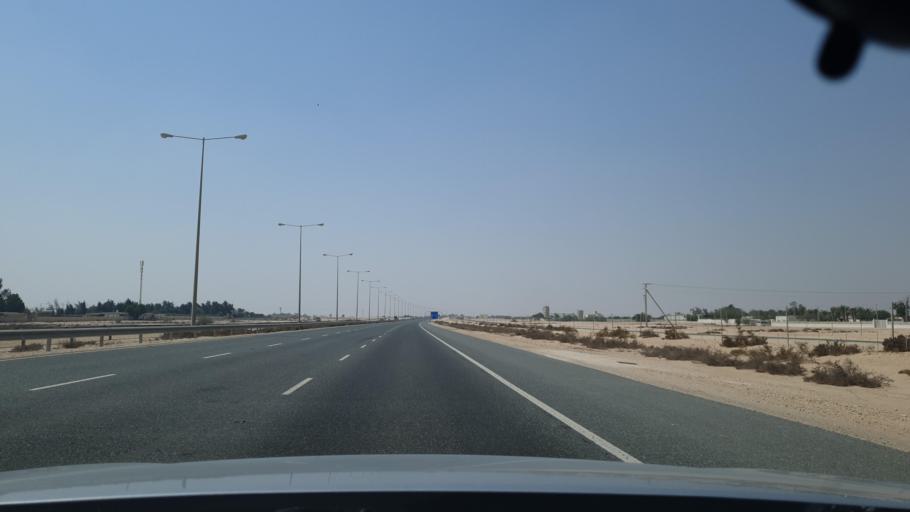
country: QA
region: Al Khawr
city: Al Khawr
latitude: 25.7553
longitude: 51.4529
